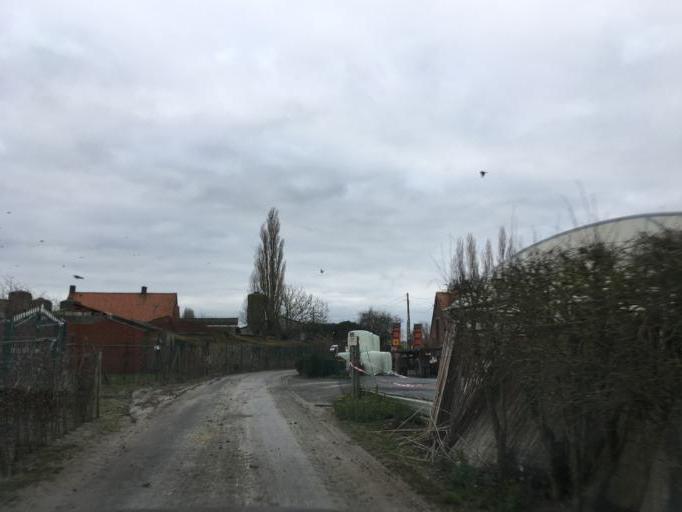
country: BE
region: Flanders
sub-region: Provincie West-Vlaanderen
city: Ledegem
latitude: 50.9007
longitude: 3.1310
